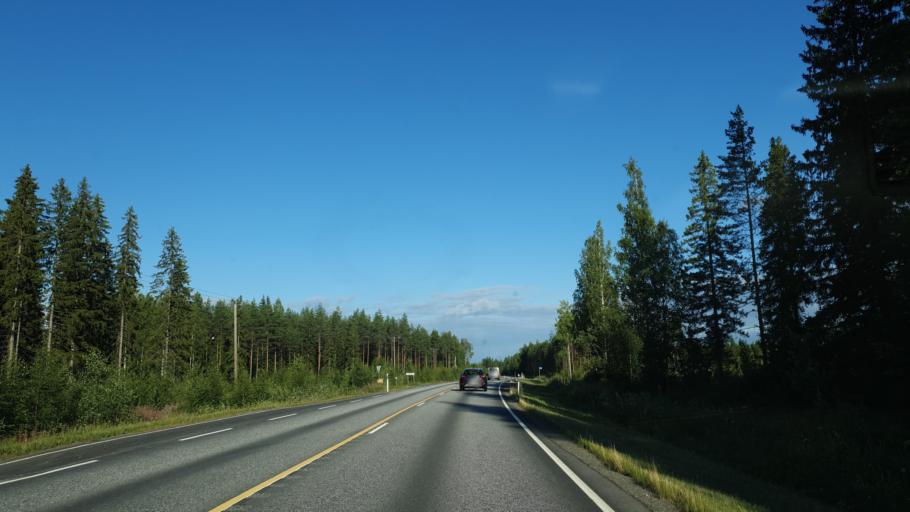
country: FI
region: North Karelia
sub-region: Joensuu
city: Outokumpu
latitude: 62.5347
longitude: 28.9495
